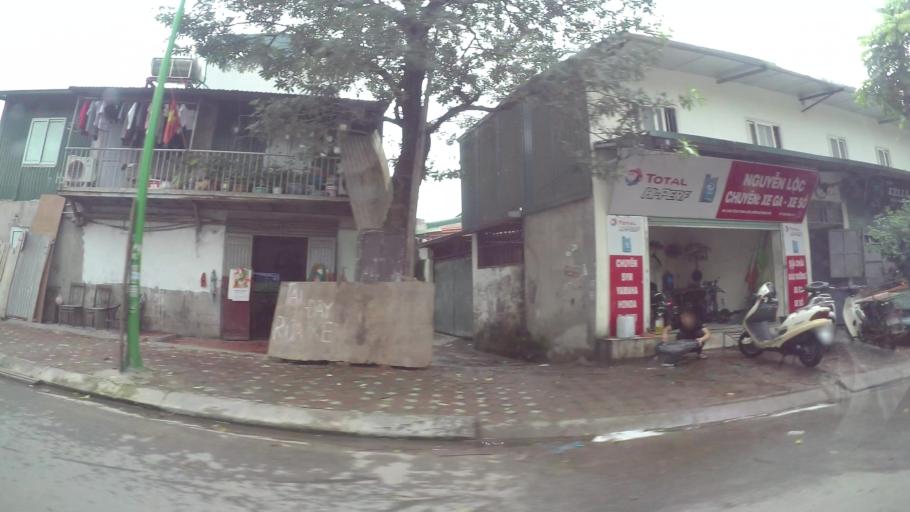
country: VN
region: Ha Noi
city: Van Dien
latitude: 20.9783
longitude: 105.8464
